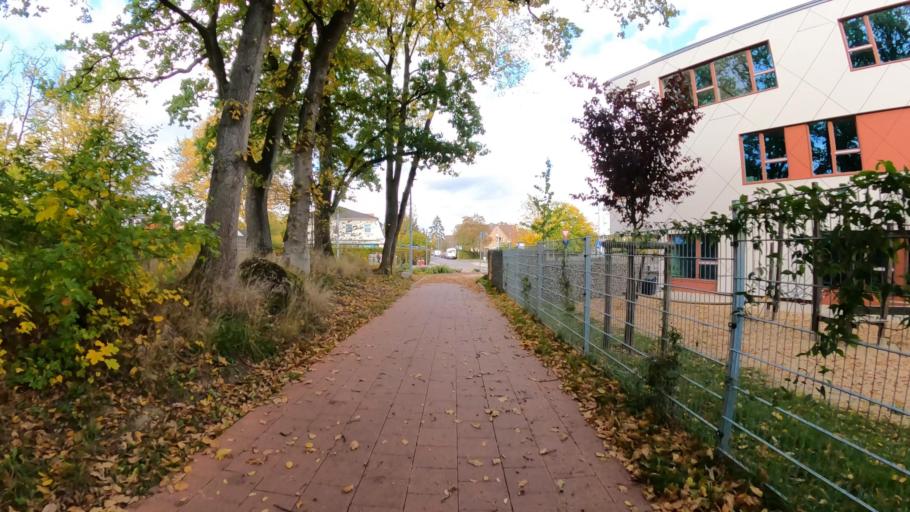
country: DE
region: Schleswig-Holstein
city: Ahrensburg
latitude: 53.6725
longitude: 10.2225
